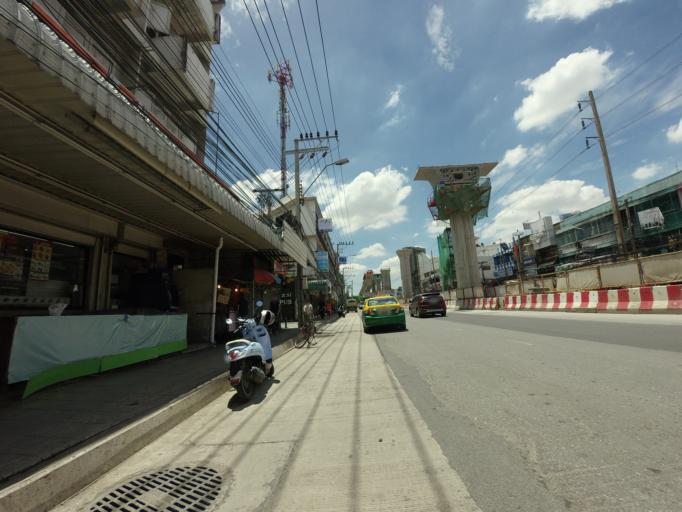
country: TH
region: Bangkok
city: Chatuchak
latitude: 13.8383
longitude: 100.5746
